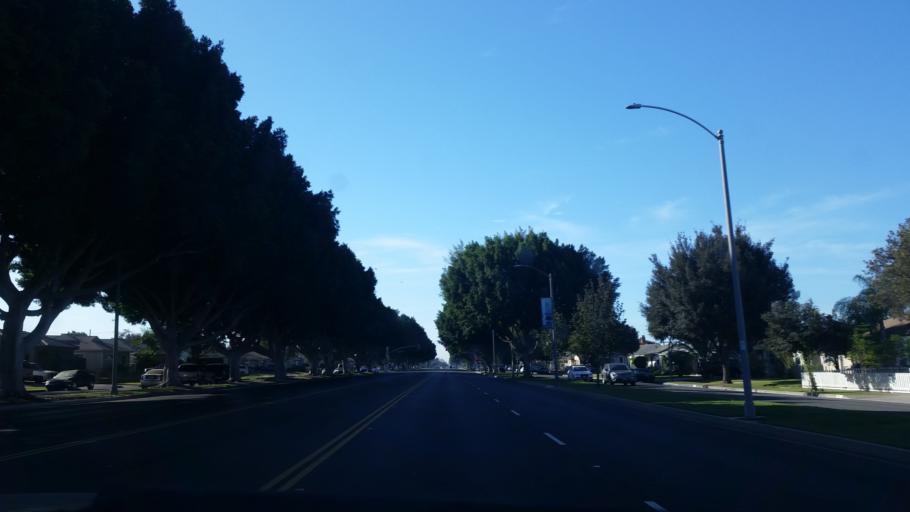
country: US
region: California
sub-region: Los Angeles County
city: Lakewood
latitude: 33.8557
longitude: -118.1251
